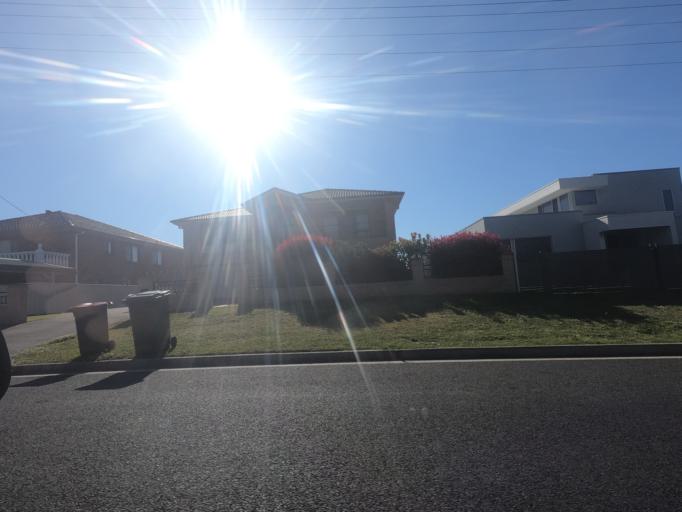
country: AU
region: New South Wales
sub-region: Wollongong
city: Corrimal
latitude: -34.3764
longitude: 150.8878
